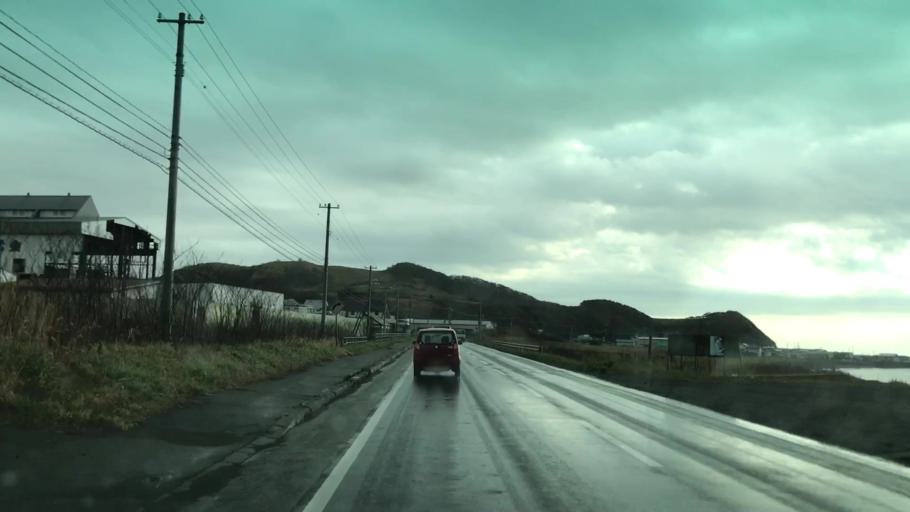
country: JP
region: Hokkaido
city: Shizunai-furukawacho
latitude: 42.1918
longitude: 142.6923
